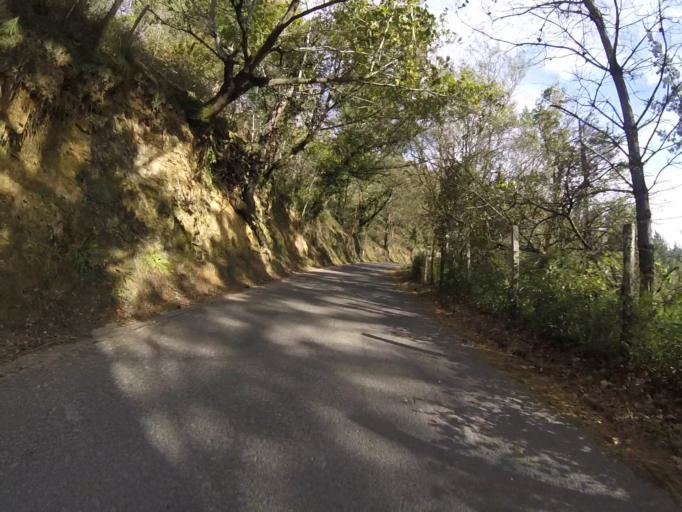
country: ES
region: Basque Country
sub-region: Provincia de Guipuzcoa
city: Orio
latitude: 43.2889
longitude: -2.0958
